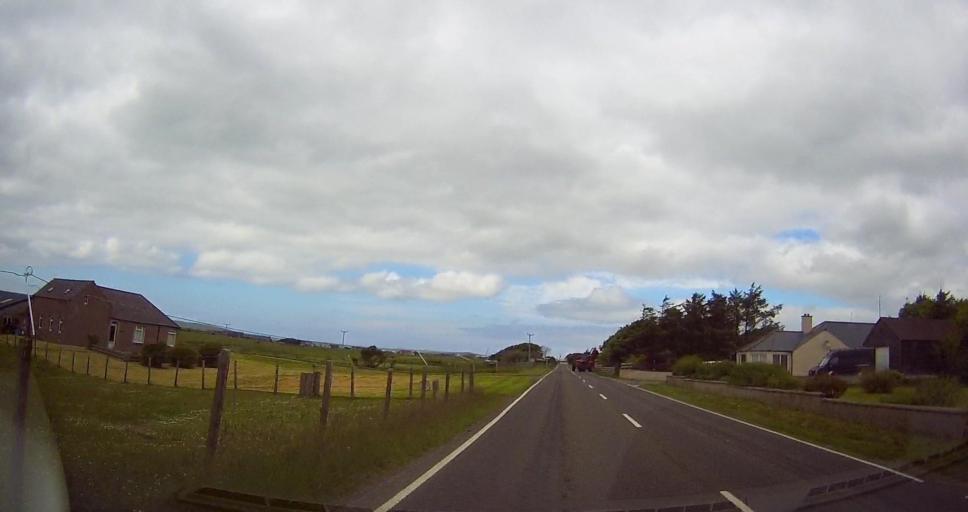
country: GB
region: Scotland
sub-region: Orkney Islands
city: Stromness
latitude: 59.0603
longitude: -3.2208
